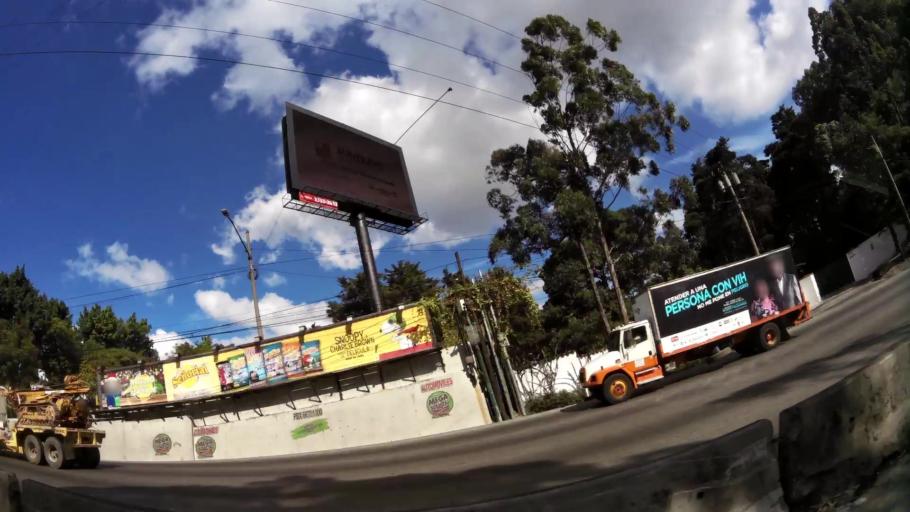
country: GT
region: Guatemala
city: Villa Nueva
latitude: 14.5622
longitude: -90.5753
